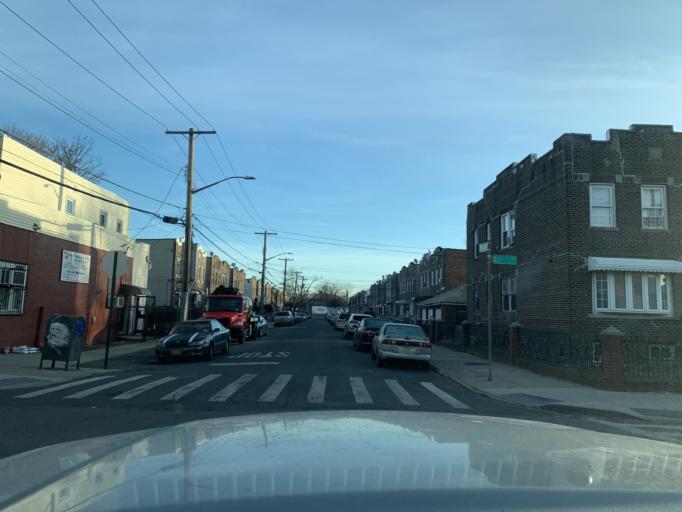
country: US
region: New York
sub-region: Queens County
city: Jamaica
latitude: 40.7029
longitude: -73.7809
